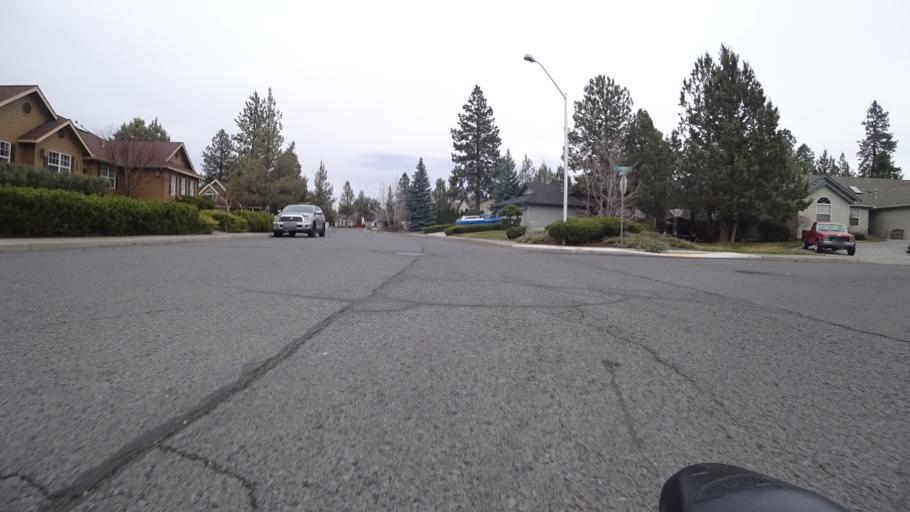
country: US
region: Oregon
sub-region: Deschutes County
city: Bend
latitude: 44.0408
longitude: -121.2773
